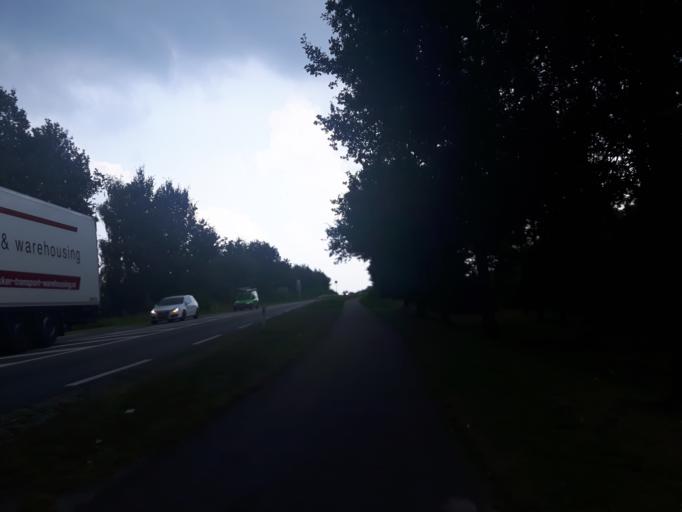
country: NL
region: Overijssel
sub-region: Gemeente Hengelo
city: Hengelo
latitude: 52.2844
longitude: 6.8533
